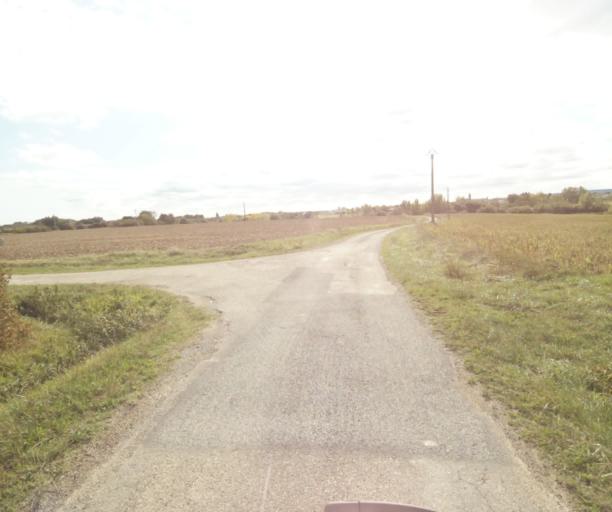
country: FR
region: Midi-Pyrenees
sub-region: Departement du Tarn-et-Garonne
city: Verdun-sur-Garonne
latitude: 43.8677
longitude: 1.1792
